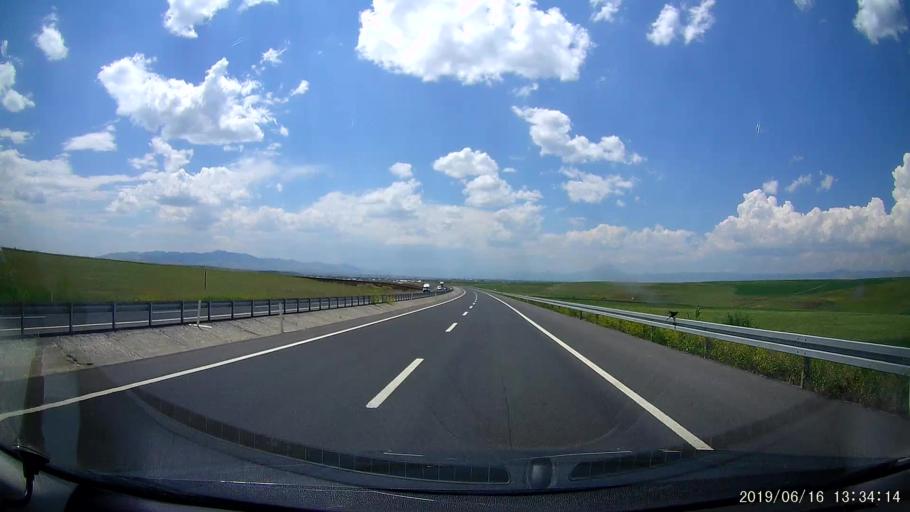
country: TR
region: Agri
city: Agri
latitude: 39.7120
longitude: 43.1322
